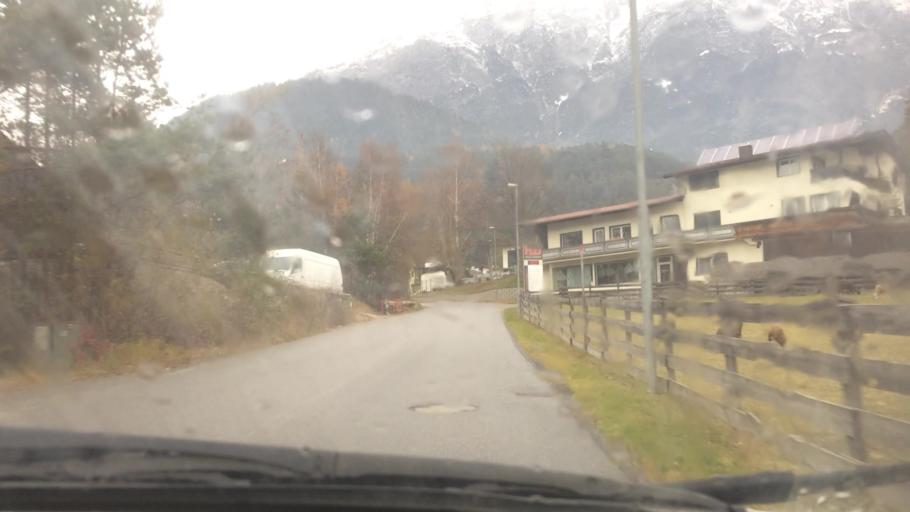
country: AT
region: Tyrol
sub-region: Politischer Bezirk Innsbruck Land
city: Pfaffenhofen
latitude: 47.3165
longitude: 11.0972
